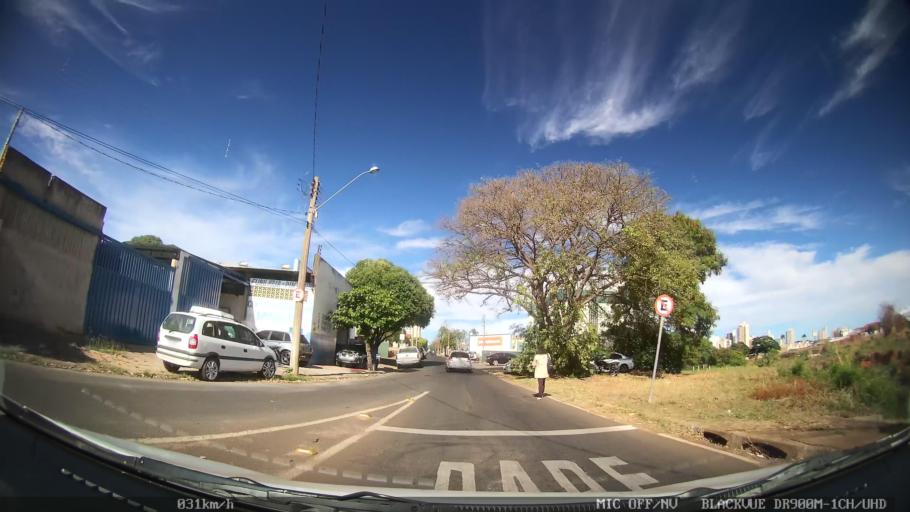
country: BR
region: Sao Paulo
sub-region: Catanduva
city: Catanduva
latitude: -21.1308
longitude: -48.9660
